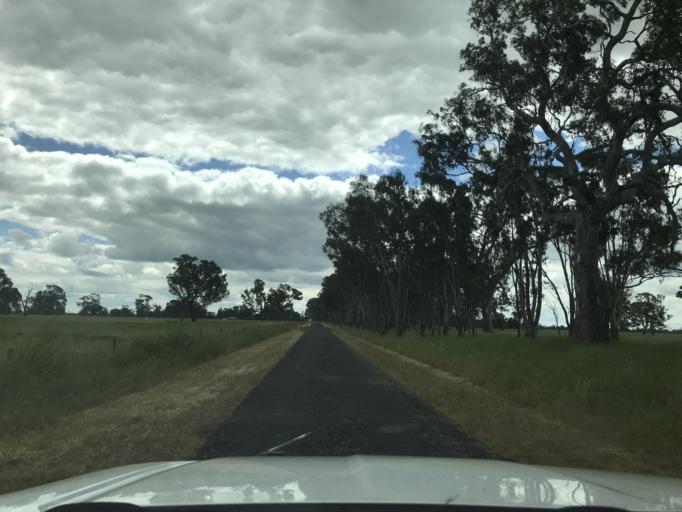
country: AU
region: South Australia
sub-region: Naracoorte and Lucindale
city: Naracoorte
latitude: -37.0743
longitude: 141.1754
